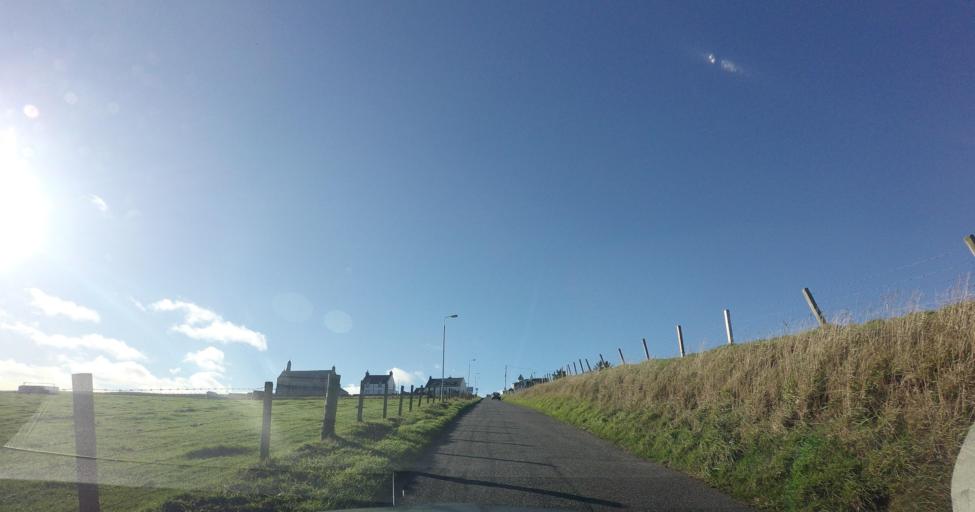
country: GB
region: Scotland
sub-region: Aberdeenshire
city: Rosehearty
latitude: 57.6773
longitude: -2.2606
